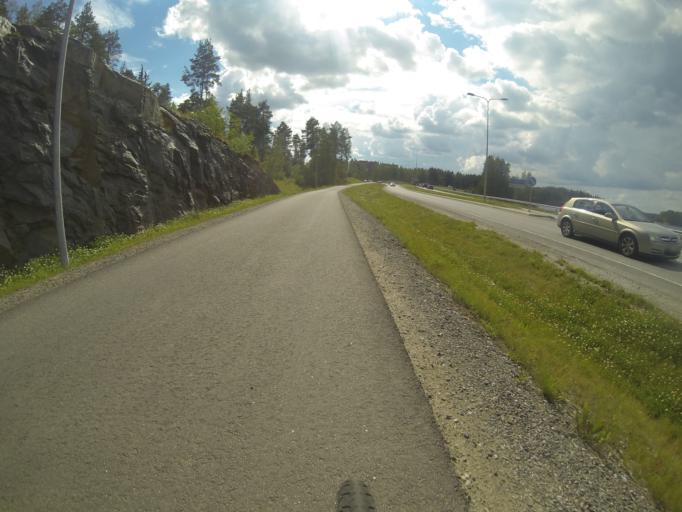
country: FI
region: Southern Savonia
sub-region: Savonlinna
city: Savonlinna
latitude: 61.8786
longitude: 28.8516
